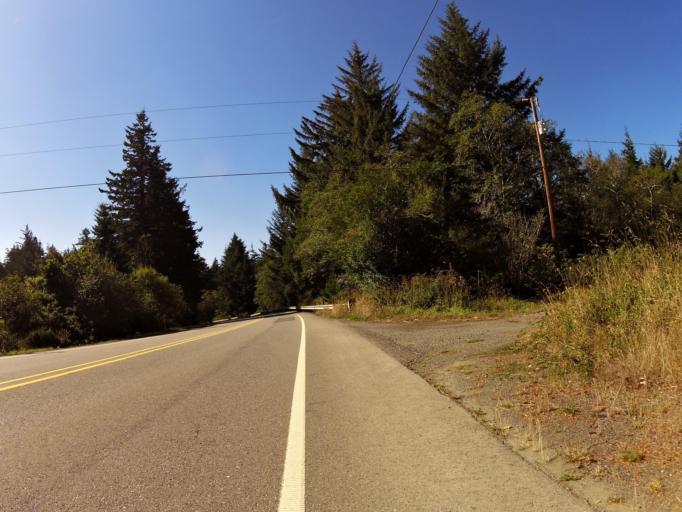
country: US
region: Oregon
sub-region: Curry County
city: Port Orford
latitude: 42.8800
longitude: -124.4671
